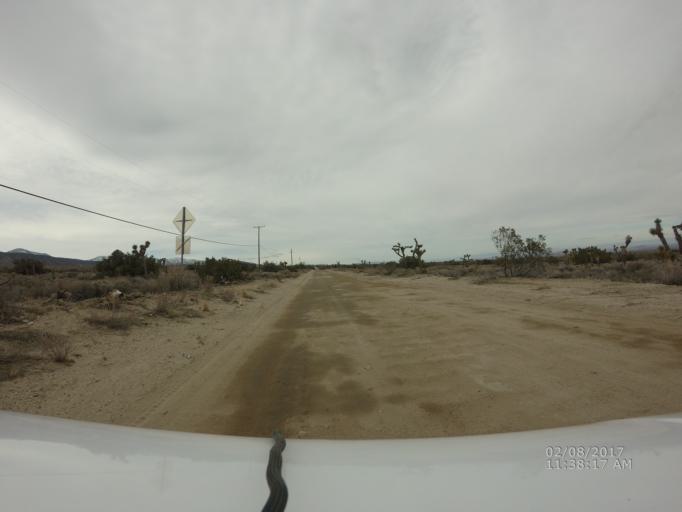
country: US
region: California
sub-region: San Bernardino County
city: Pinon Hills
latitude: 34.4695
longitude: -117.7144
